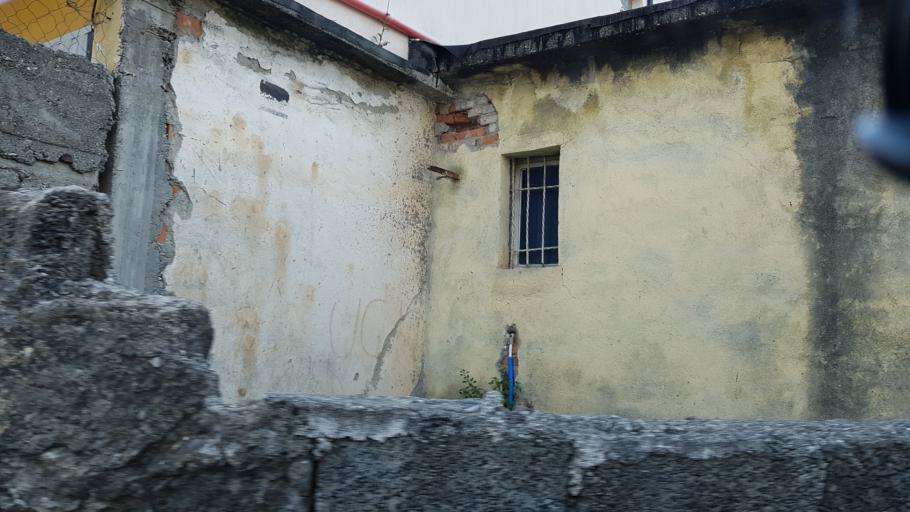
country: AL
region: Shkoder
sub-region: Rrethi i Shkodres
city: Shkoder
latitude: 42.0619
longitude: 19.5079
